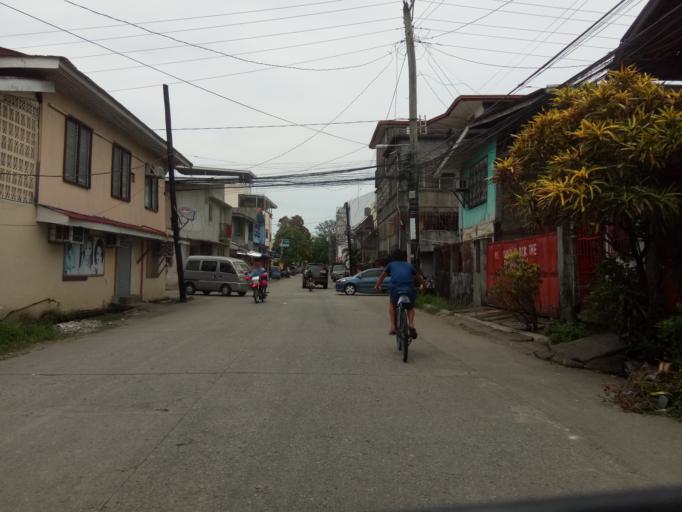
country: PH
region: Caraga
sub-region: Province of Surigao del Norte
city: Surigao
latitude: 9.7869
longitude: 125.4902
